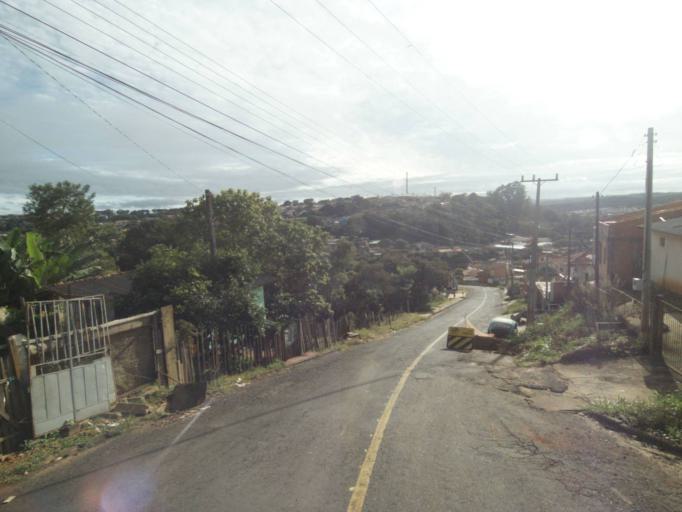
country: BR
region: Parana
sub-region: Telemaco Borba
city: Telemaco Borba
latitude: -24.3418
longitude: -50.6175
